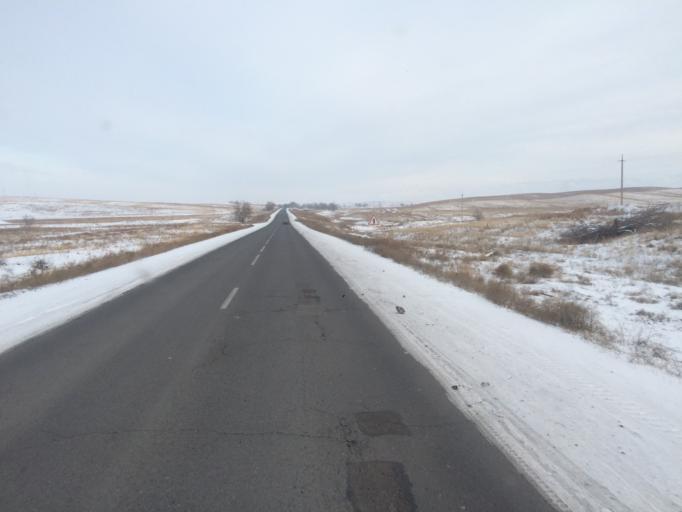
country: KG
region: Chuy
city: Bystrovka
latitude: 43.3212
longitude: 75.9870
